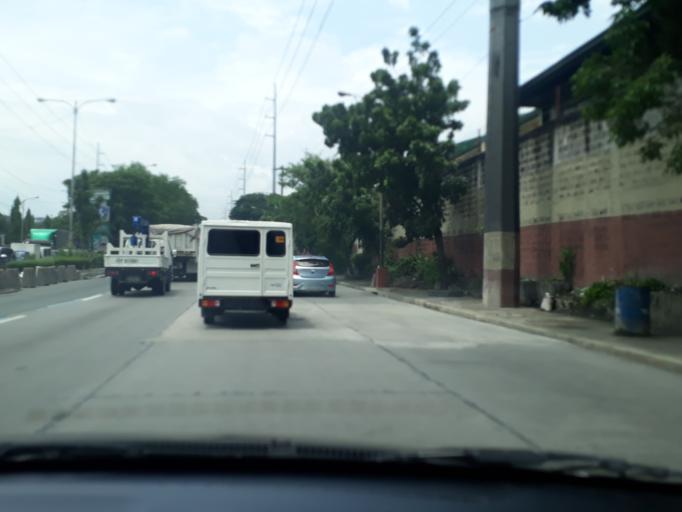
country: PH
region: Metro Manila
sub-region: Pasig
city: Pasig City
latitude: 14.5764
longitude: 121.0728
